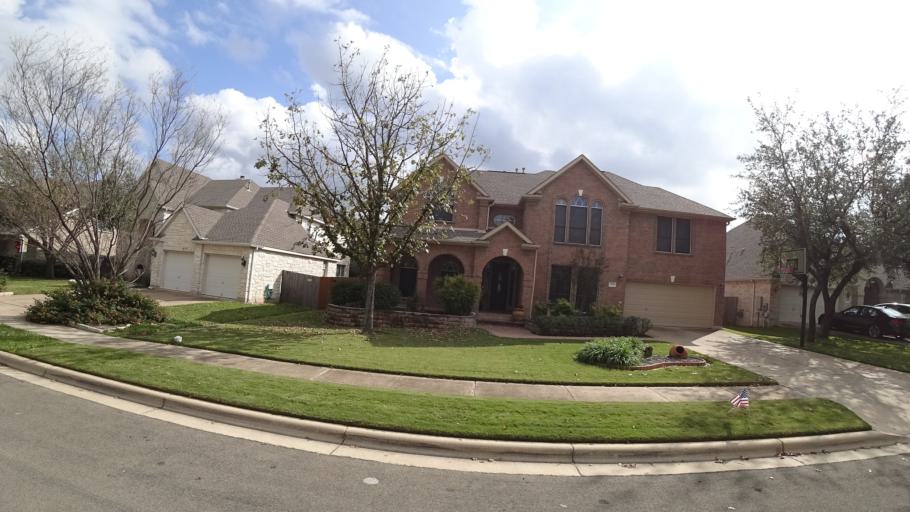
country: US
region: Texas
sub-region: Williamson County
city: Anderson Mill
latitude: 30.4251
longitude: -97.8604
